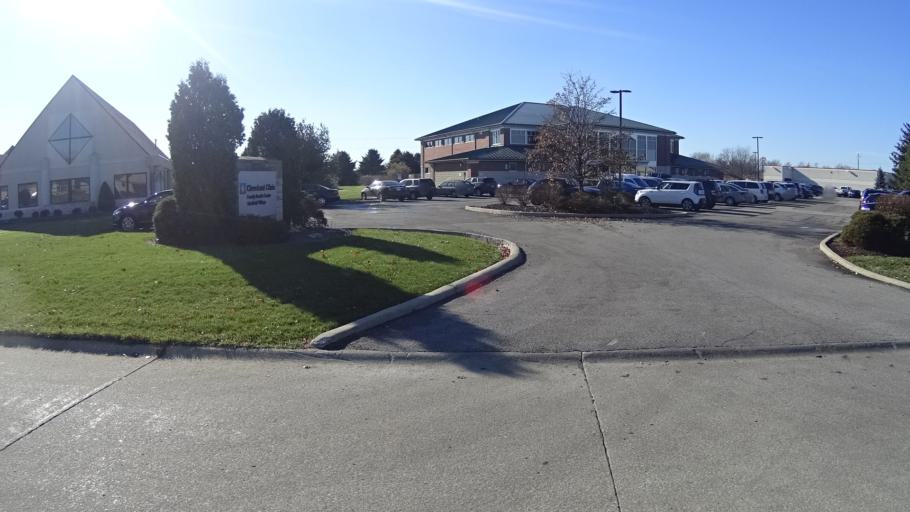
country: US
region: Ohio
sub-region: Lorain County
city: Sheffield
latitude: 41.4206
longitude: -82.0746
